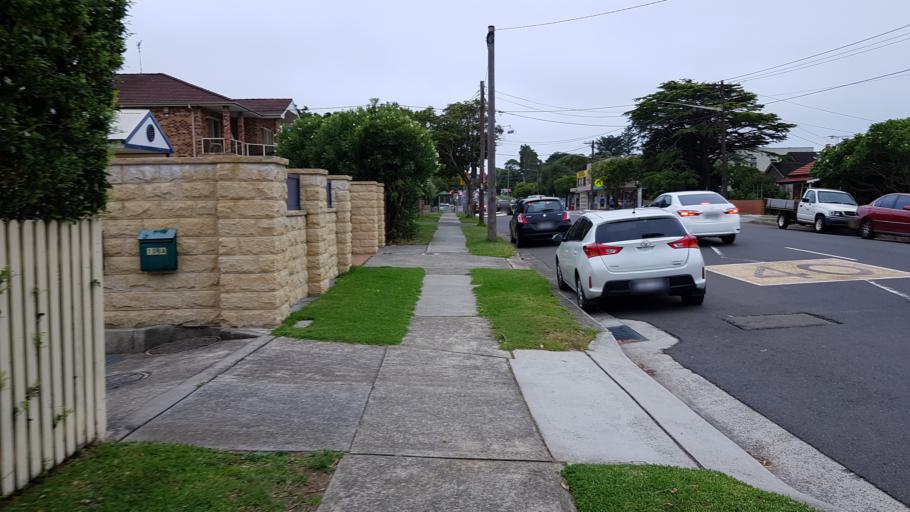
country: AU
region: New South Wales
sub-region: Warringah
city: Narraweena
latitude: -33.7515
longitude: 151.2743
